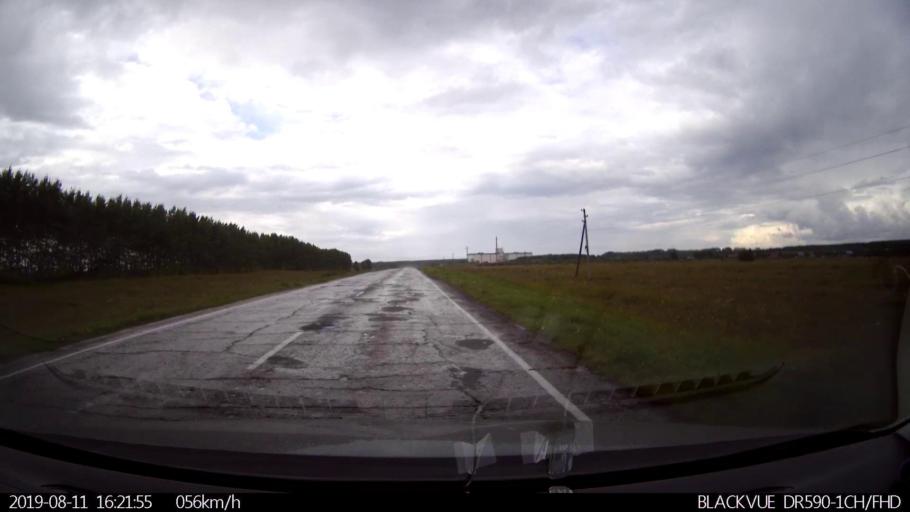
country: RU
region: Ulyanovsk
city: Mayna
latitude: 54.0836
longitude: 47.5956
